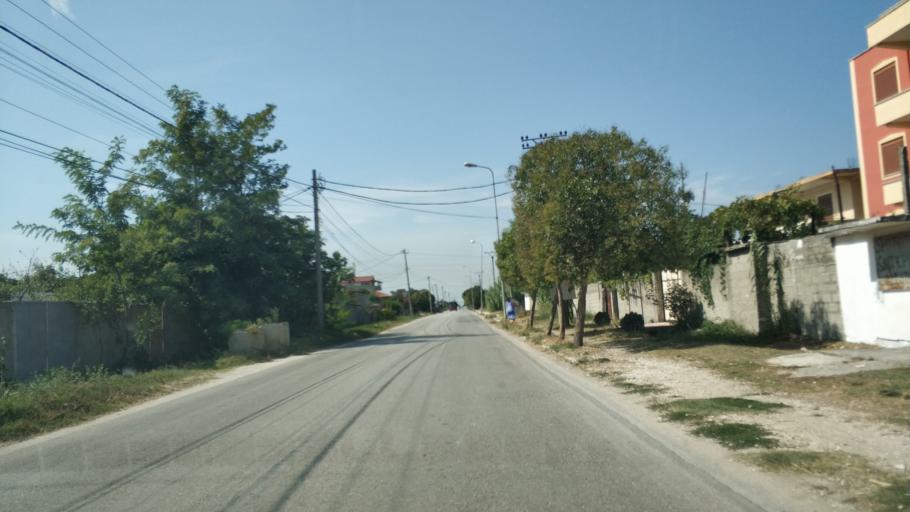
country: AL
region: Fier
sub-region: Rrethi i Fierit
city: Dermenas
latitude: 40.7438
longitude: 19.4981
